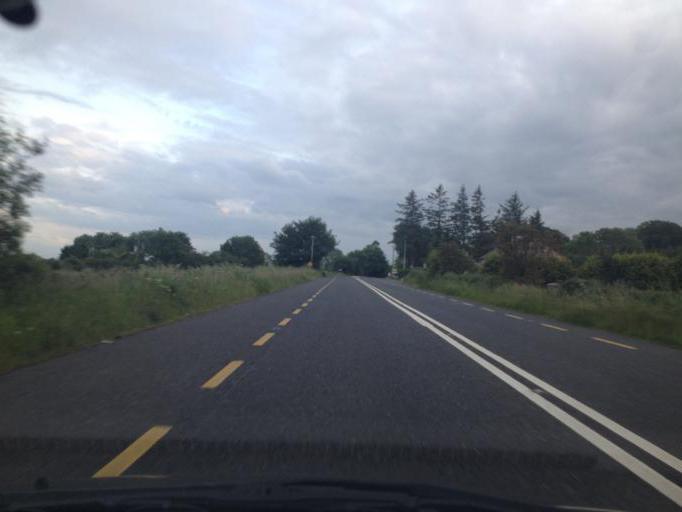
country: IE
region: Connaught
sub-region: Sligo
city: Sligo
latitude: 54.3000
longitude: -8.4723
